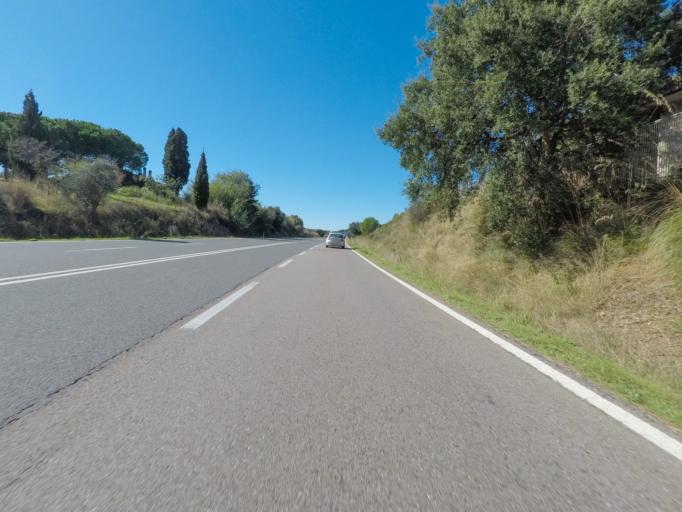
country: IT
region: Tuscany
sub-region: Provincia di Grosseto
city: Orbetello Scalo
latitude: 42.4164
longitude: 11.3134
